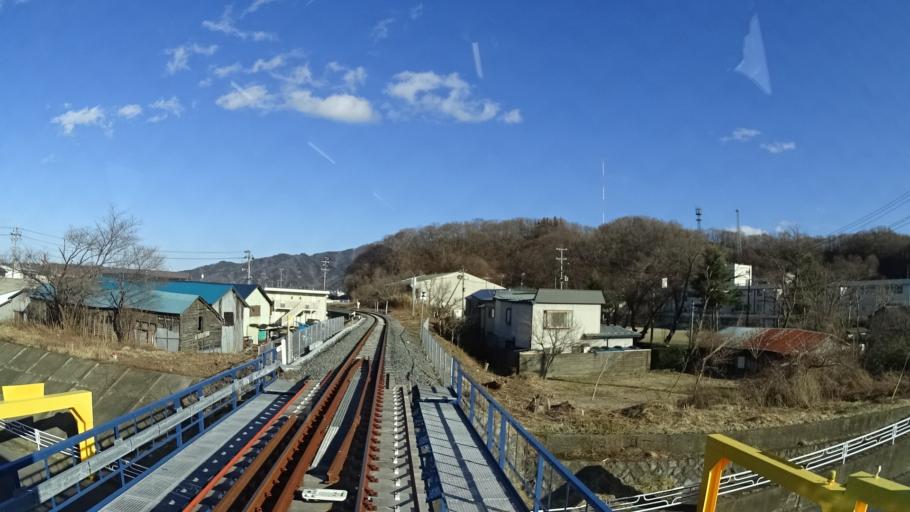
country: JP
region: Iwate
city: Miyako
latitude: 39.6377
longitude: 141.9559
